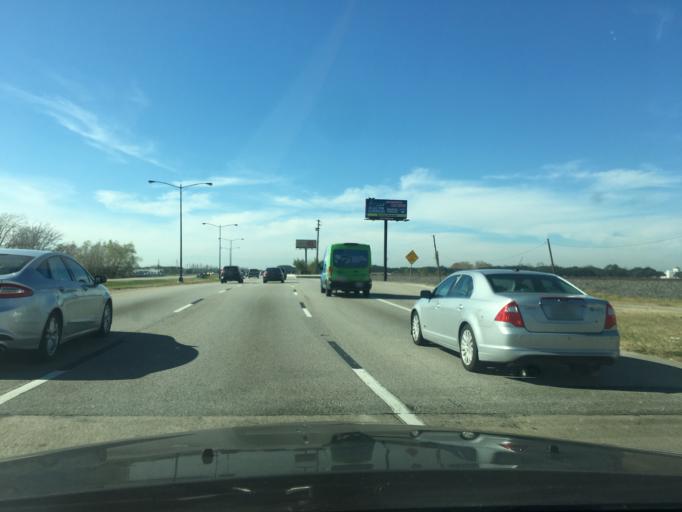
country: US
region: Texas
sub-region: Fort Bend County
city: Sugar Land
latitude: 29.6128
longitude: -95.6510
